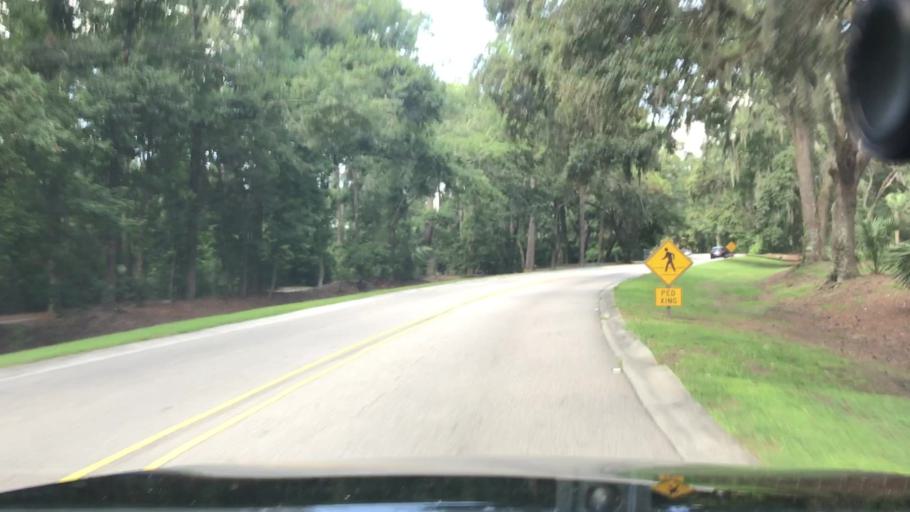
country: US
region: South Carolina
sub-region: Beaufort County
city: Hilton Head Island
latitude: 32.1473
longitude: -80.7809
